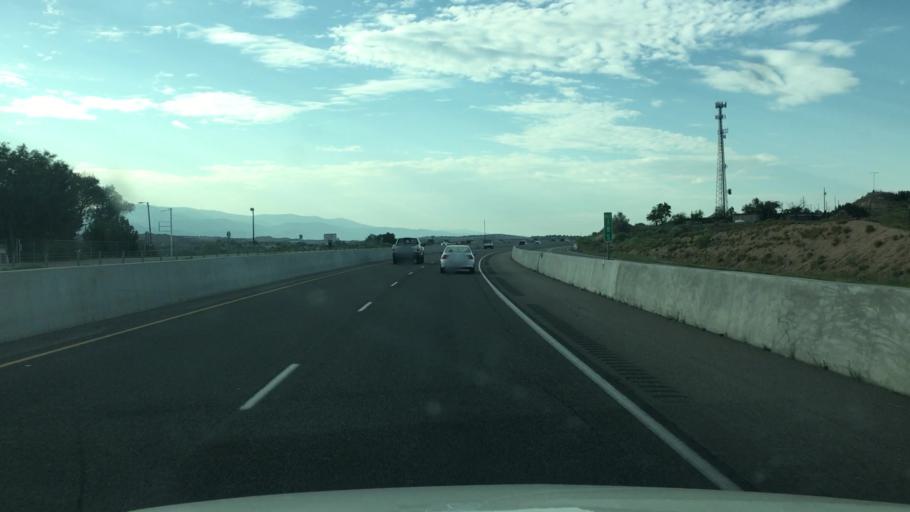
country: US
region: New Mexico
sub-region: Santa Fe County
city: El Valle de Arroyo Seco
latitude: 35.9572
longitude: -106.0231
